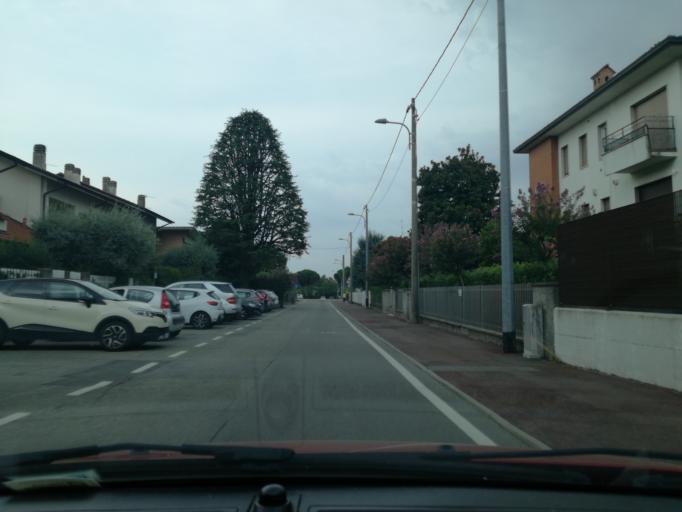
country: IT
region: Lombardy
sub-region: Provincia di Monza e Brianza
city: Carnate
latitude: 45.6516
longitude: 9.3749
